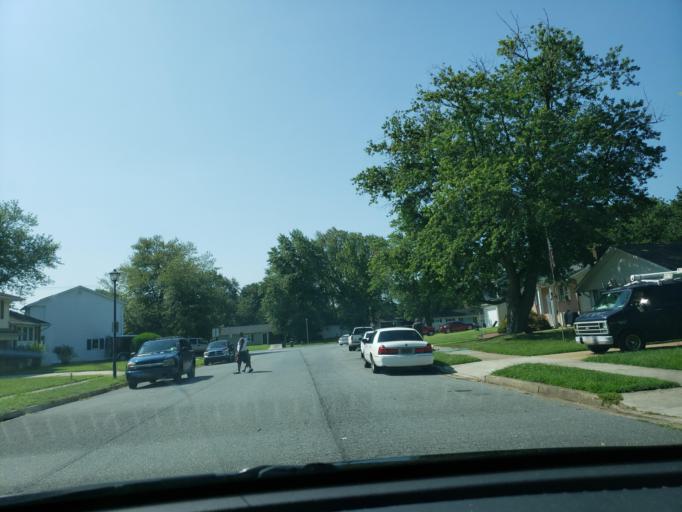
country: US
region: Delaware
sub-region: Kent County
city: Rodney Village
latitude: 39.1337
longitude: -75.5337
